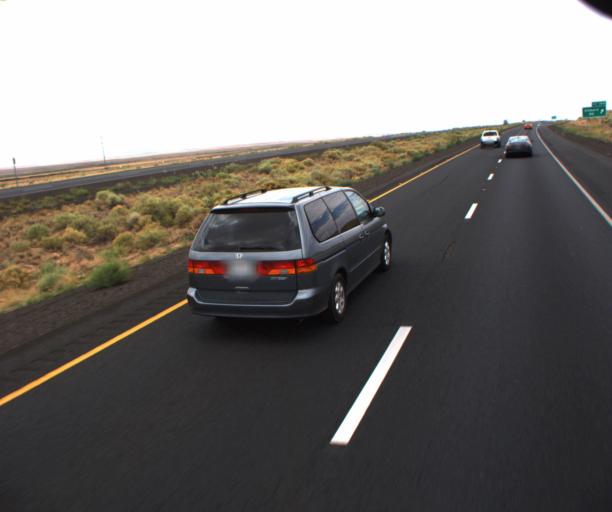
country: US
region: Arizona
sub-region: Navajo County
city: Joseph City
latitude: 34.9740
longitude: -110.5174
